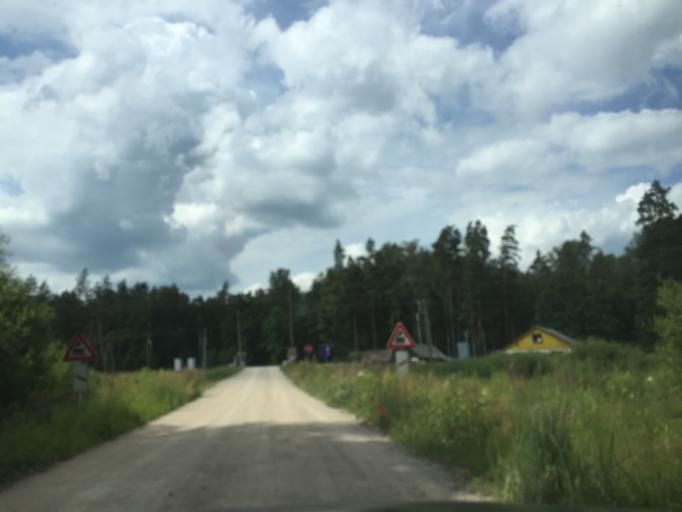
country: LV
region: Jelgava
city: Jelgava
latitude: 56.6261
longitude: 23.6629
